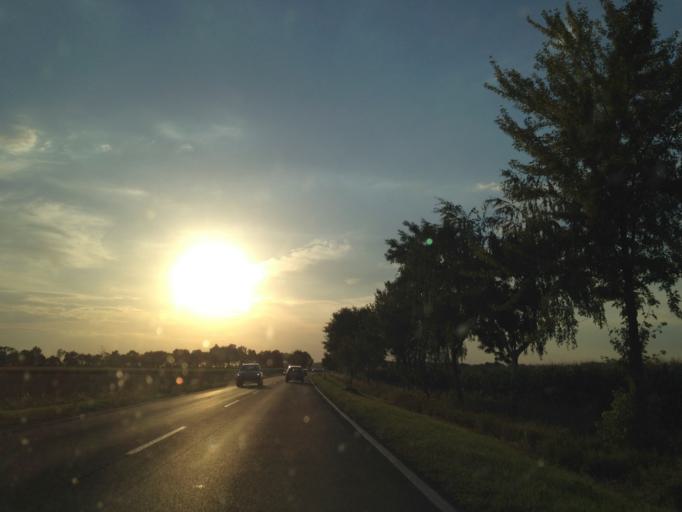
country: HU
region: Gyor-Moson-Sopron
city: Kimle
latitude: 47.8172
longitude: 17.3403
